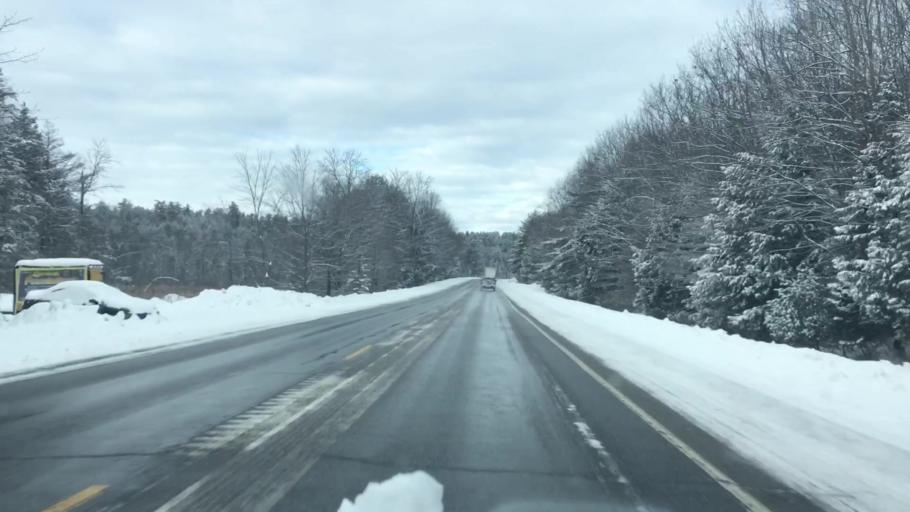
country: US
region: Maine
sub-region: Cumberland County
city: Bridgton
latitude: 44.0063
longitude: -70.6721
